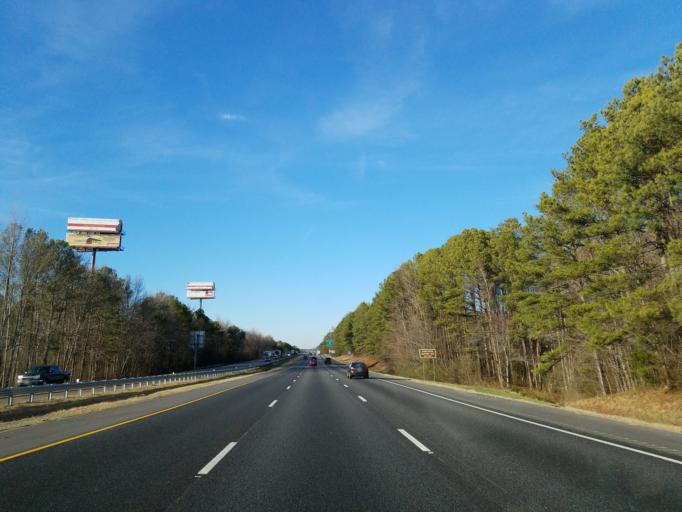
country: US
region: Georgia
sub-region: Gordon County
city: Calhoun
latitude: 34.5195
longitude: -84.9189
